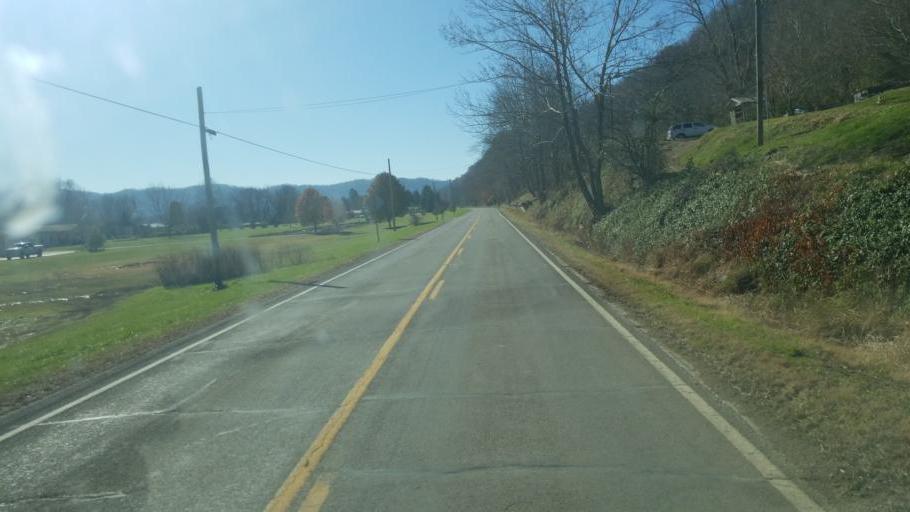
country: US
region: Kentucky
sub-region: Lewis County
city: Vanceburg
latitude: 38.6257
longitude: -83.2628
